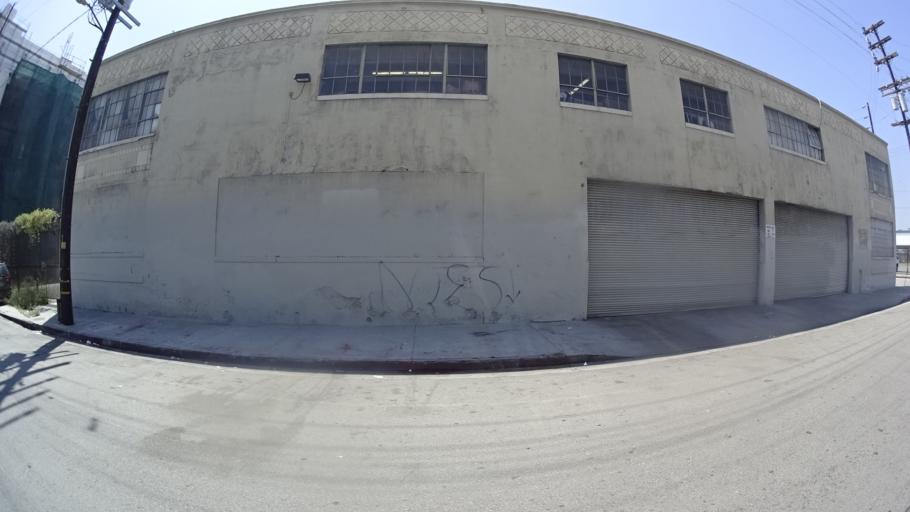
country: US
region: California
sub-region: Los Angeles County
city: Los Angeles
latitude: 34.0355
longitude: -118.2347
